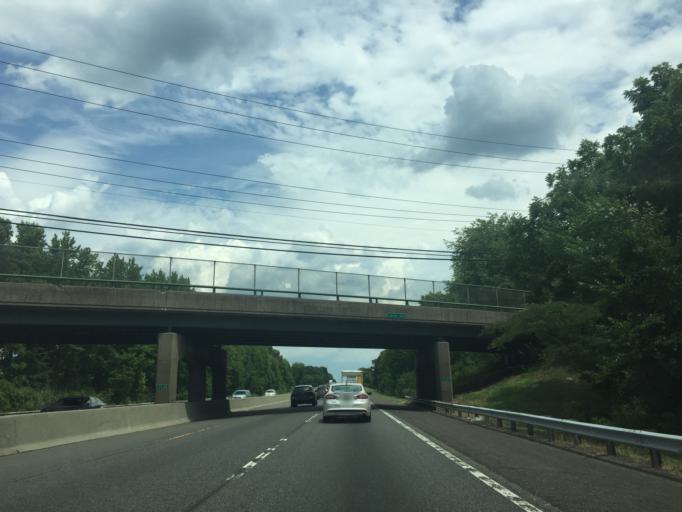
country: US
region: New Jersey
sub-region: Camden County
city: Barrington
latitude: 39.8637
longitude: -75.0515
